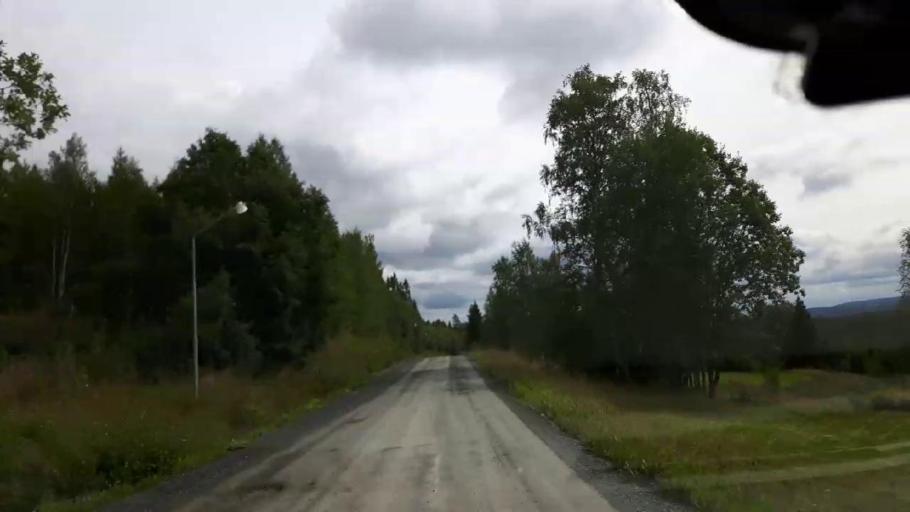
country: SE
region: Jaemtland
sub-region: Krokoms Kommun
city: Valla
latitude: 63.6233
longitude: 14.0528
